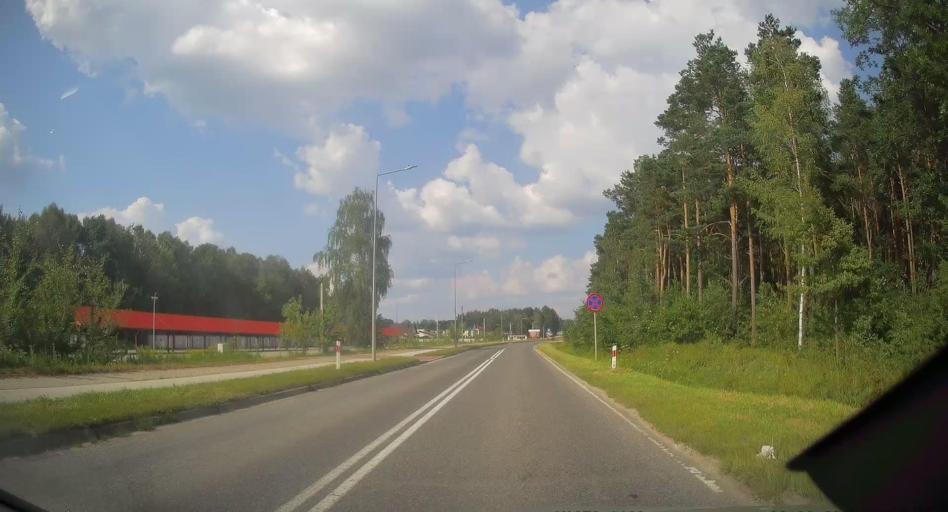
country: PL
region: Swietokrzyskie
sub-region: Powiat kielecki
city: Lopuszno
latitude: 50.9358
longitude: 20.2414
